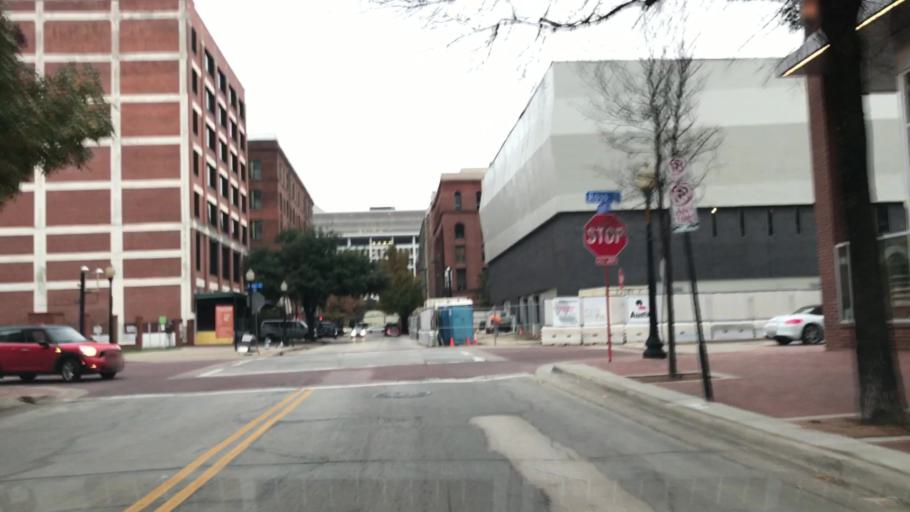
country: US
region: Texas
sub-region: Dallas County
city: Dallas
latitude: 32.7816
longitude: -96.8078
